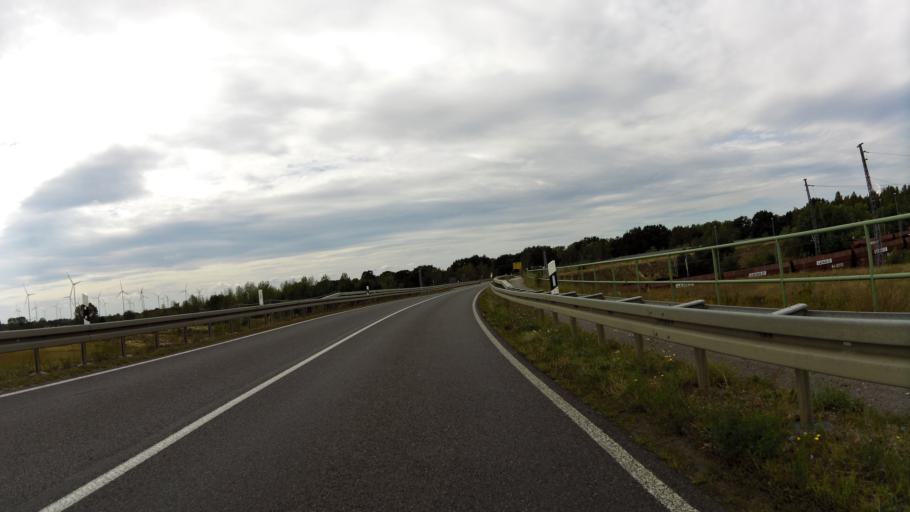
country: DE
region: Brandenburg
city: Heinersbruck
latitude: 51.8049
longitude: 14.4935
